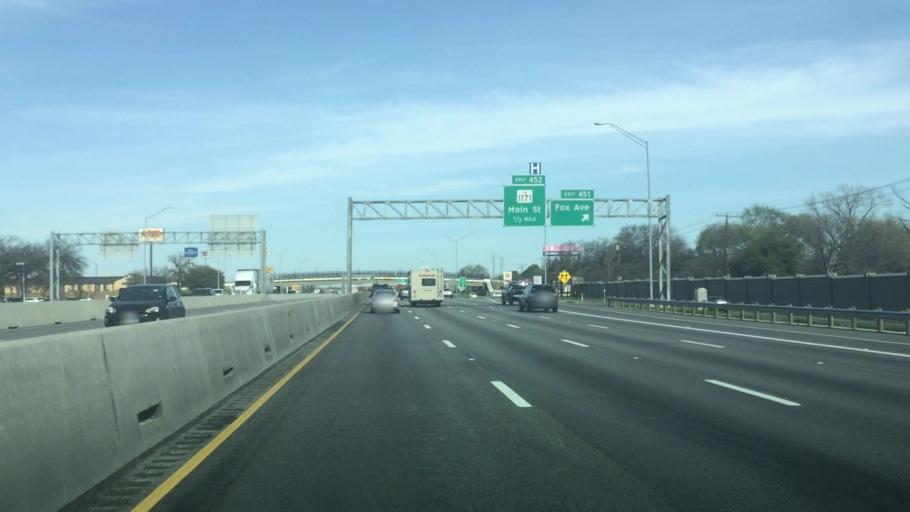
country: US
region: Texas
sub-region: Denton County
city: Lewisville
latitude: 33.0354
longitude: -96.9987
